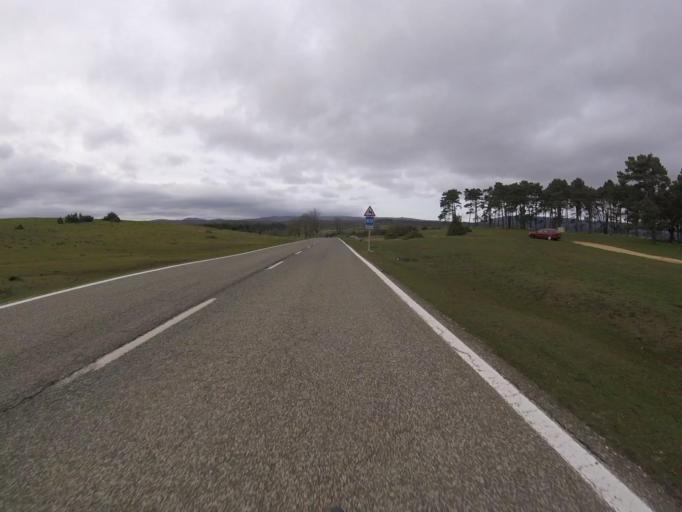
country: ES
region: Navarre
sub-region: Provincia de Navarra
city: Eulate
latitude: 42.8088
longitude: -2.1547
